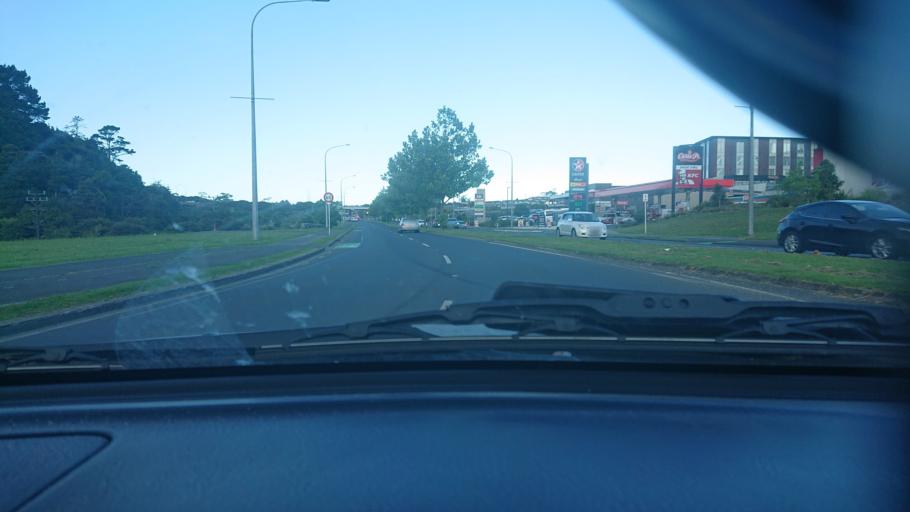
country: NZ
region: Auckland
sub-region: Auckland
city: Rothesay Bay
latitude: -36.7205
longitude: 174.7088
